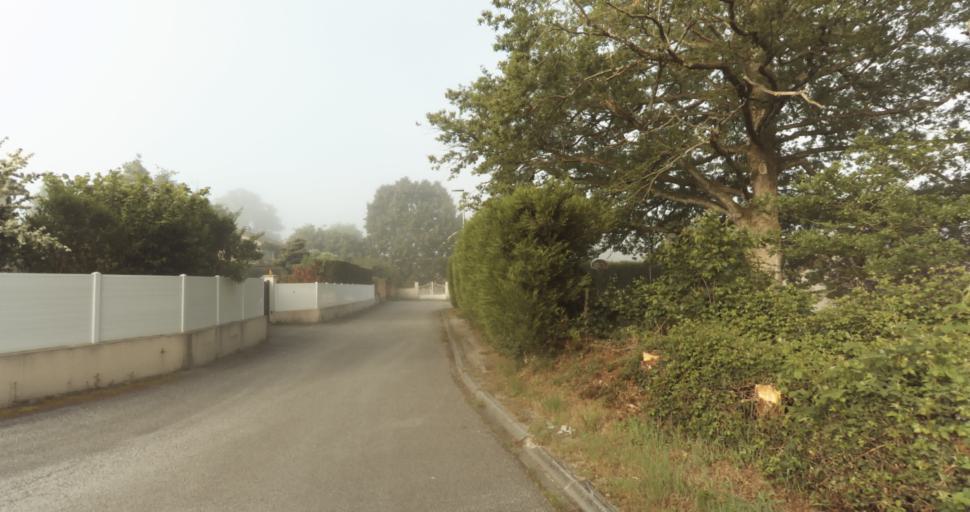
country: FR
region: Limousin
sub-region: Departement de la Haute-Vienne
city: Condat-sur-Vienne
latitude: 45.7872
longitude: 1.2824
